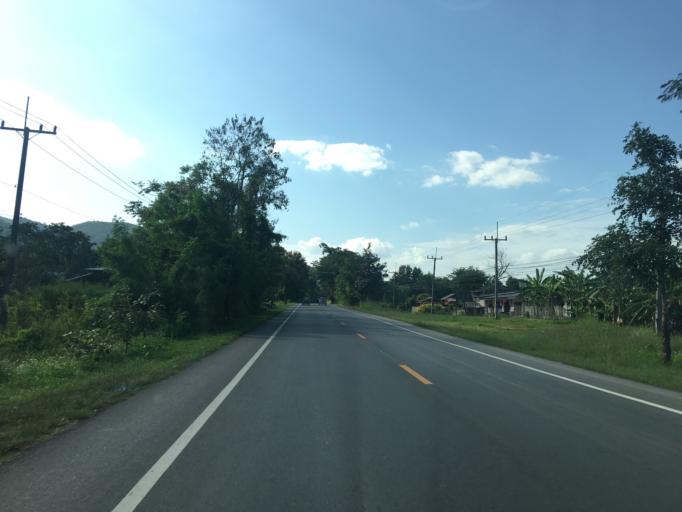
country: TH
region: Phayao
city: Chun
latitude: 19.3509
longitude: 100.1069
